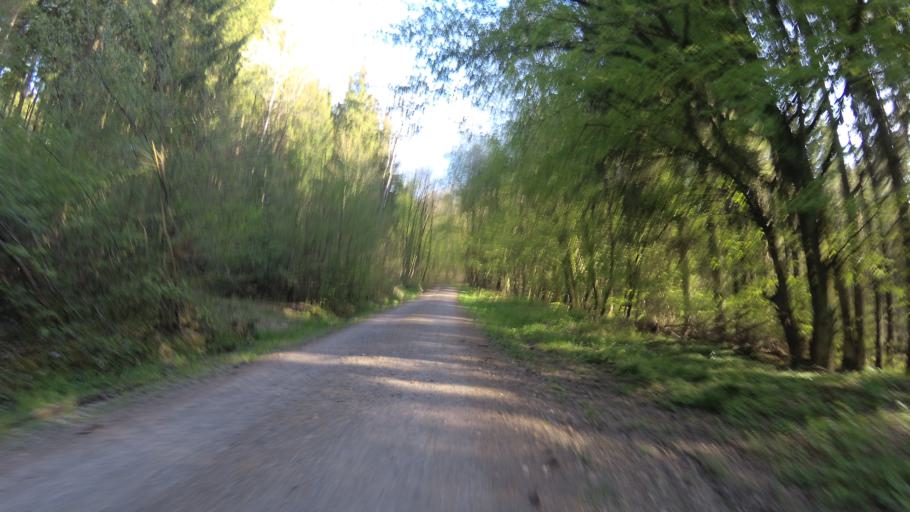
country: DE
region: Saarland
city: Mainzweiler
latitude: 49.4272
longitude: 7.1296
